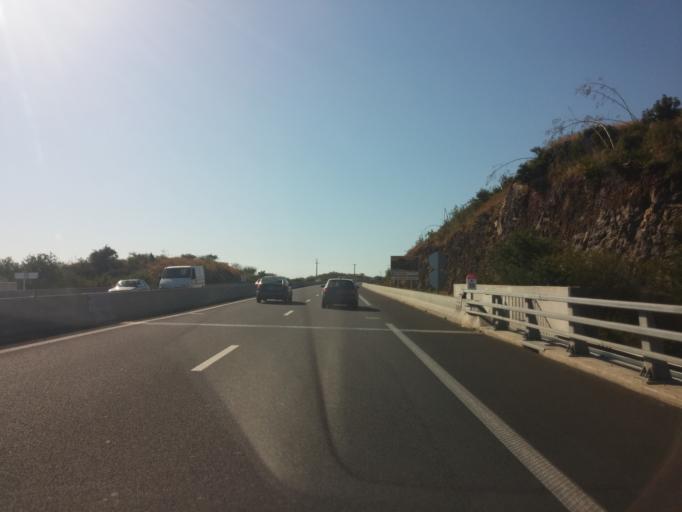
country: RE
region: Reunion
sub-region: Reunion
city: Saint-Paul
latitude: -21.0524
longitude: 55.2488
